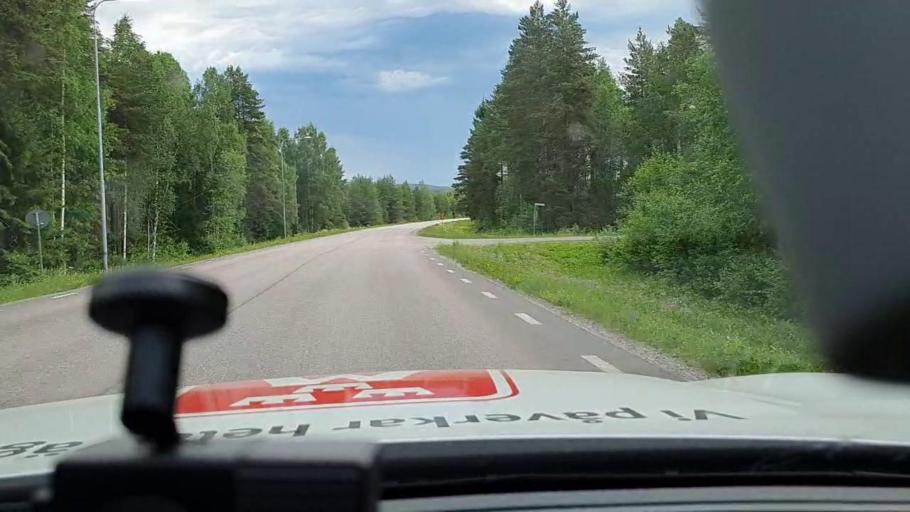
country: SE
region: Norrbotten
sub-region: Bodens Kommun
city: Boden
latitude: 65.8177
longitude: 21.5879
